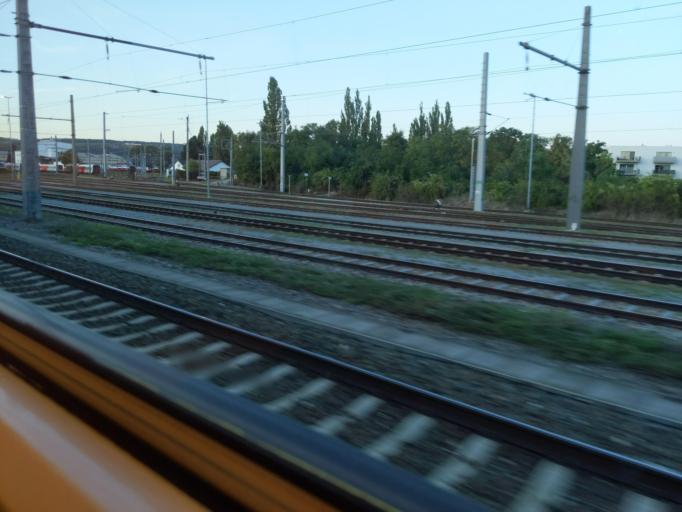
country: AT
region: Lower Austria
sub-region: Politischer Bezirk Korneuburg
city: Langenzersdorf
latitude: 48.2758
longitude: 16.3939
